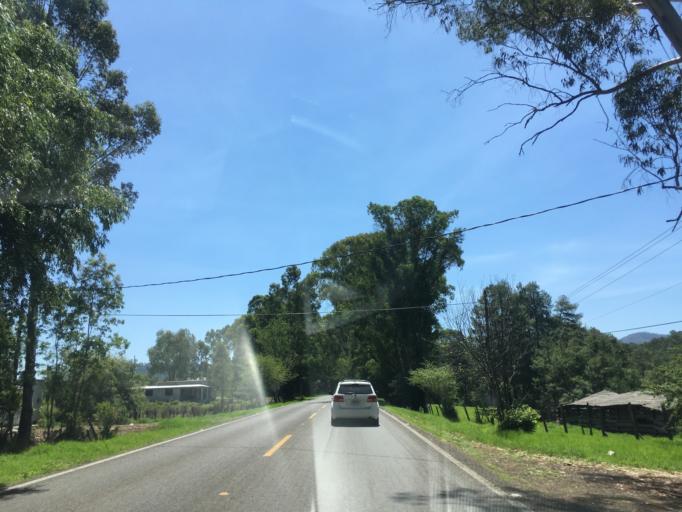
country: MX
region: Michoacan
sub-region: Hidalgo
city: Tierras Coloradas (San Pedro)
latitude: 19.6686
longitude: -100.6974
